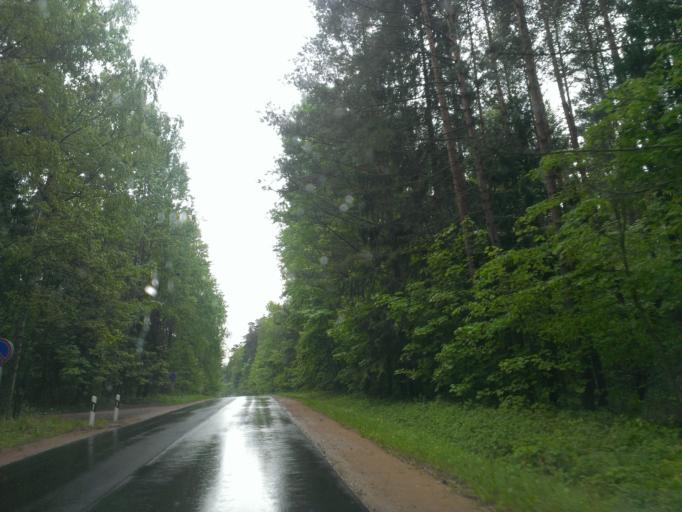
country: LT
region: Klaipedos apskritis
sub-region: Klaipeda
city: Klaipeda
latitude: 55.7870
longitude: 21.0748
